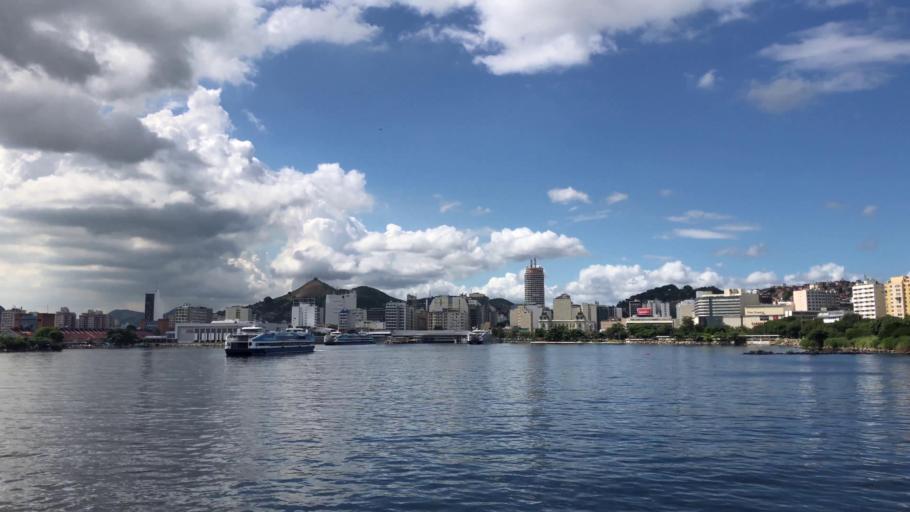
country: BR
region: Rio de Janeiro
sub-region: Niteroi
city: Niteroi
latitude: -22.8938
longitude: -43.1283
